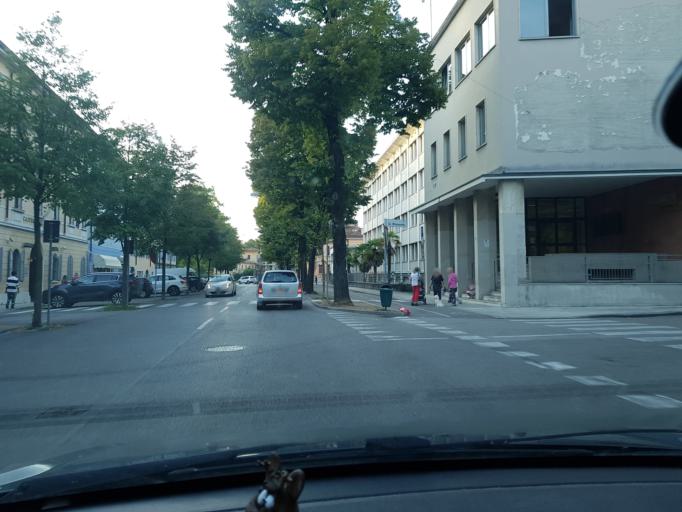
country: IT
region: Friuli Venezia Giulia
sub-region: Provincia di Gorizia
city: Gorizia
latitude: 45.9435
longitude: 13.6187
